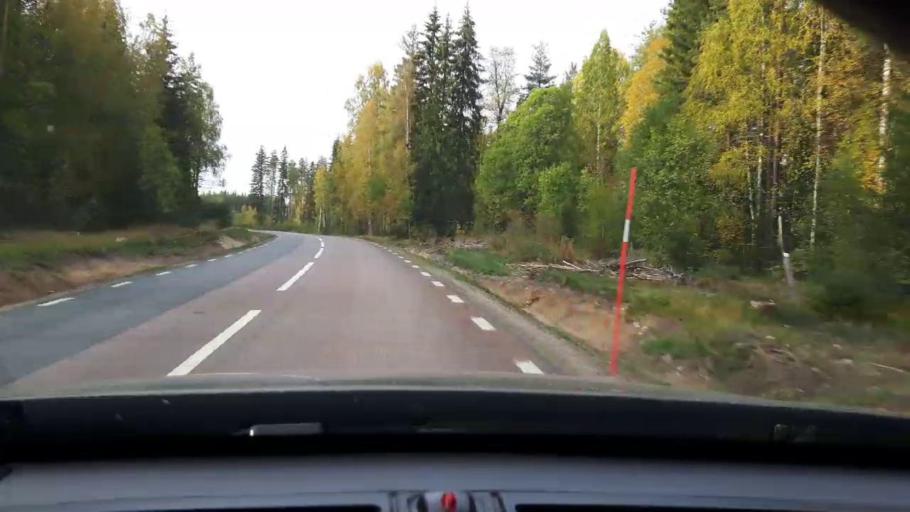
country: SE
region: Dalarna
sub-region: Gagnefs Kommun
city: Mockfjard
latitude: 60.3198
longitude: 14.9386
